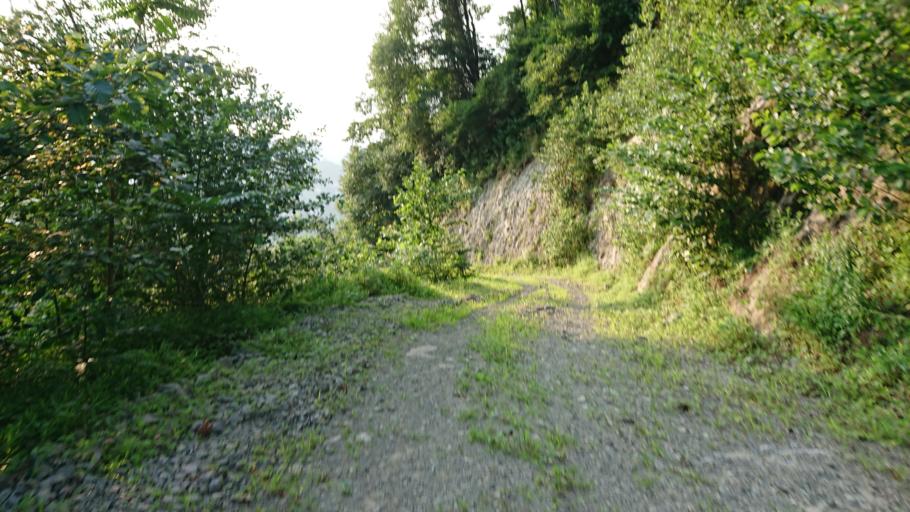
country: TR
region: Rize
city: Rize
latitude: 40.9910
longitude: 40.5017
